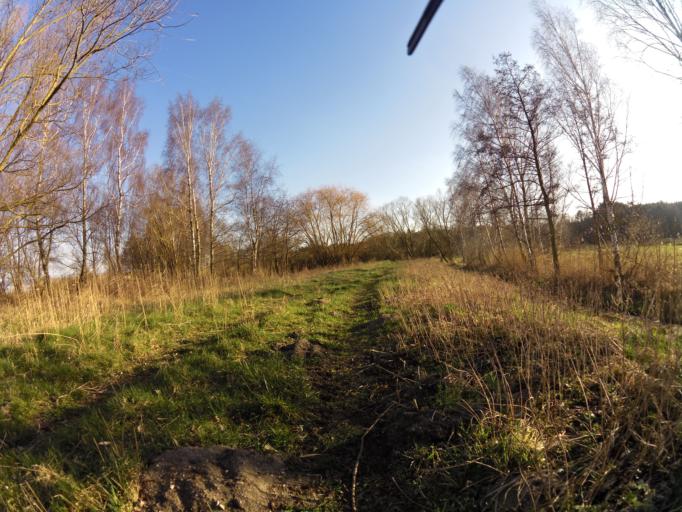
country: PL
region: West Pomeranian Voivodeship
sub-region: Powiat policki
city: Nowe Warpno
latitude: 53.7211
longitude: 14.3386
